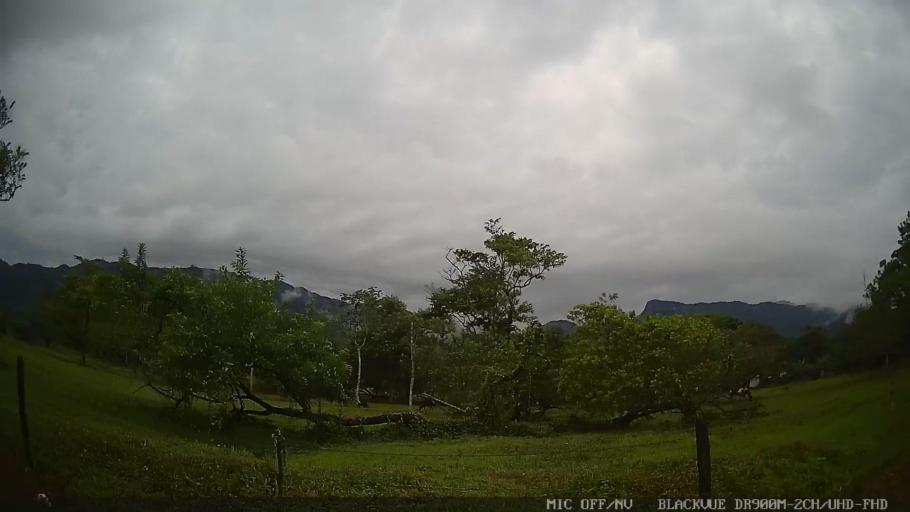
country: BR
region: Sao Paulo
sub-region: Sao Sebastiao
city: Sao Sebastiao
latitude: -23.7197
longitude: -45.4509
